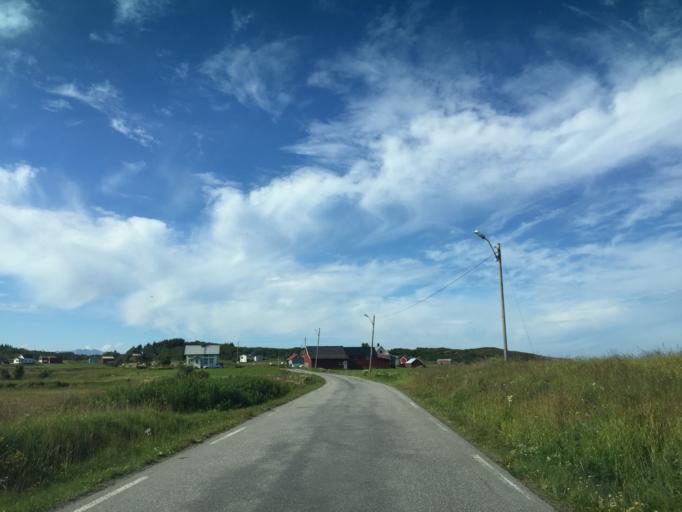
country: NO
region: Nordland
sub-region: Vagan
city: Kabelvag
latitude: 68.3933
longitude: 14.4619
